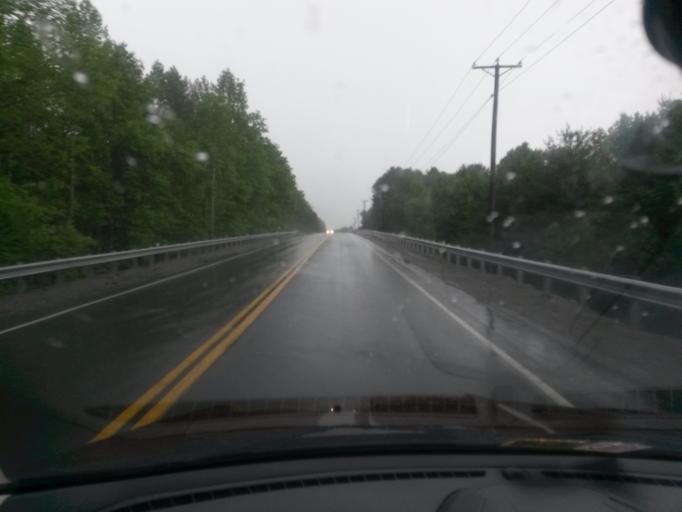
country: US
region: Virginia
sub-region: Floyd County
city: Floyd
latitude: 36.9810
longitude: -80.4034
